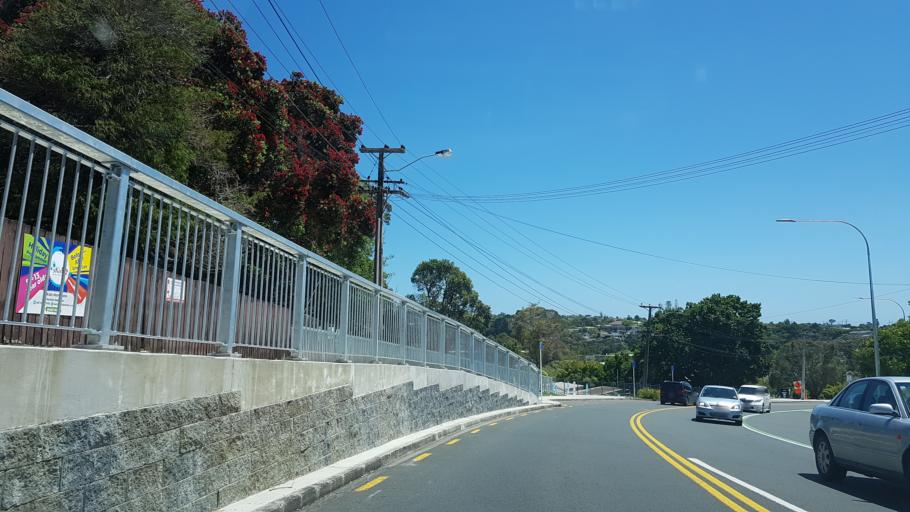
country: NZ
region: Auckland
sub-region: Auckland
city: North Shore
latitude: -36.8100
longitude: 174.7434
